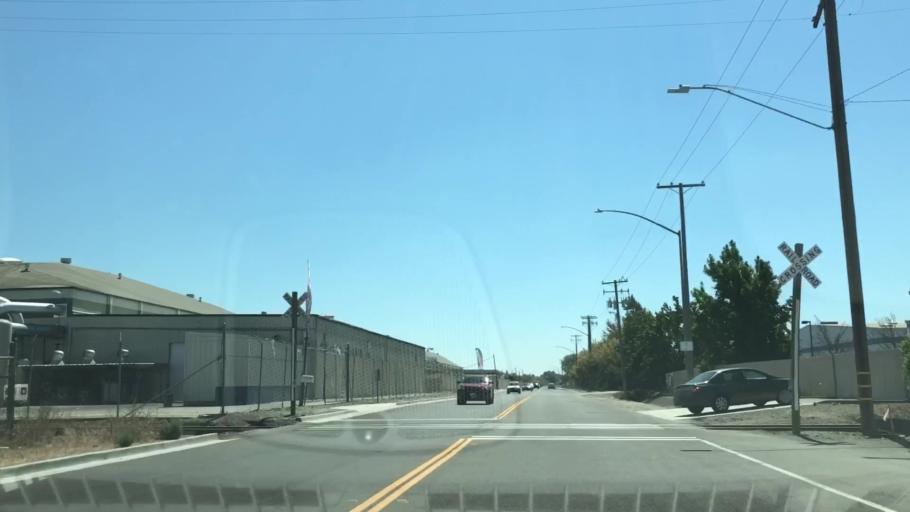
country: US
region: California
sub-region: San Joaquin County
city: Stockton
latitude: 37.9364
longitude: -121.3184
